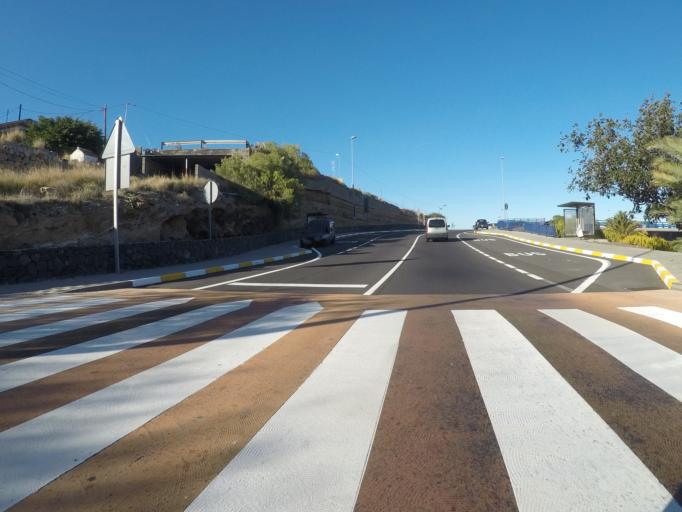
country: ES
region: Canary Islands
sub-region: Provincia de Santa Cruz de Tenerife
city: Candelaria
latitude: 28.3597
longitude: -16.3728
